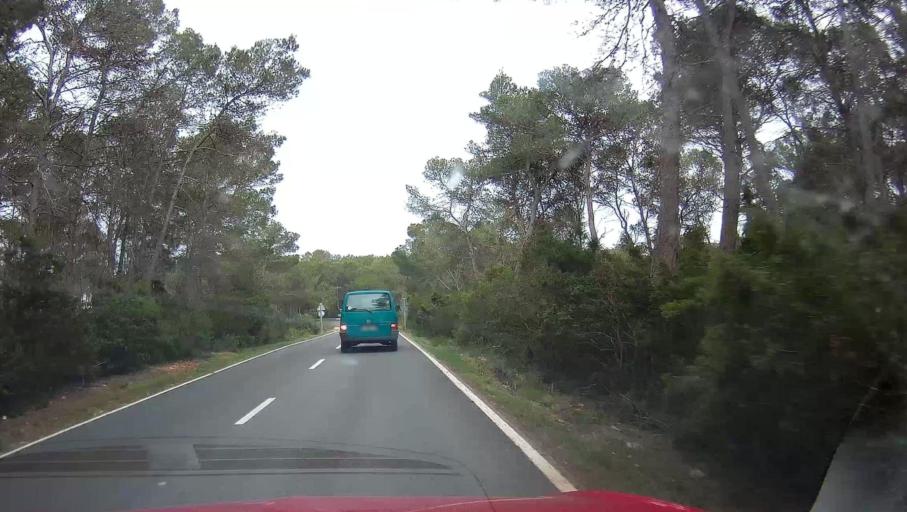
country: ES
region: Balearic Islands
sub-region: Illes Balears
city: Sant Joan de Labritja
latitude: 39.0475
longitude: 1.4093
